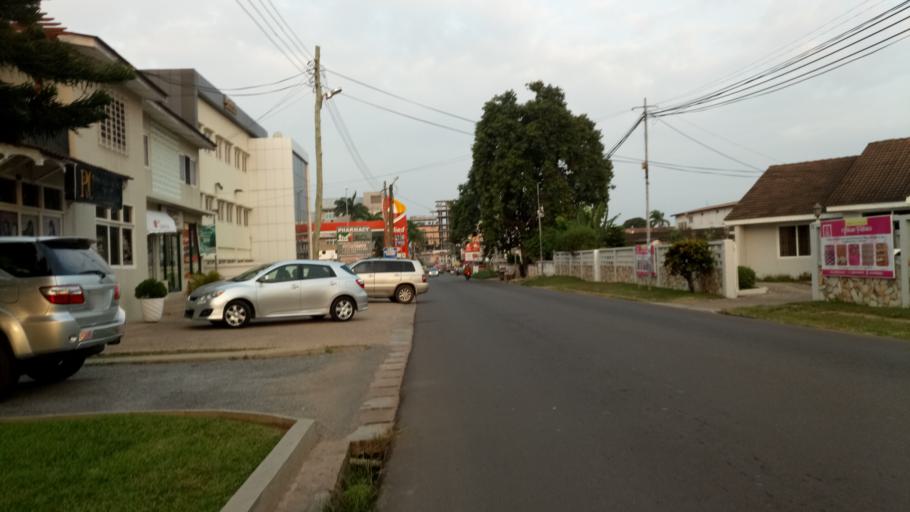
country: GH
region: Greater Accra
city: Accra
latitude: 5.5663
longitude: -0.1841
